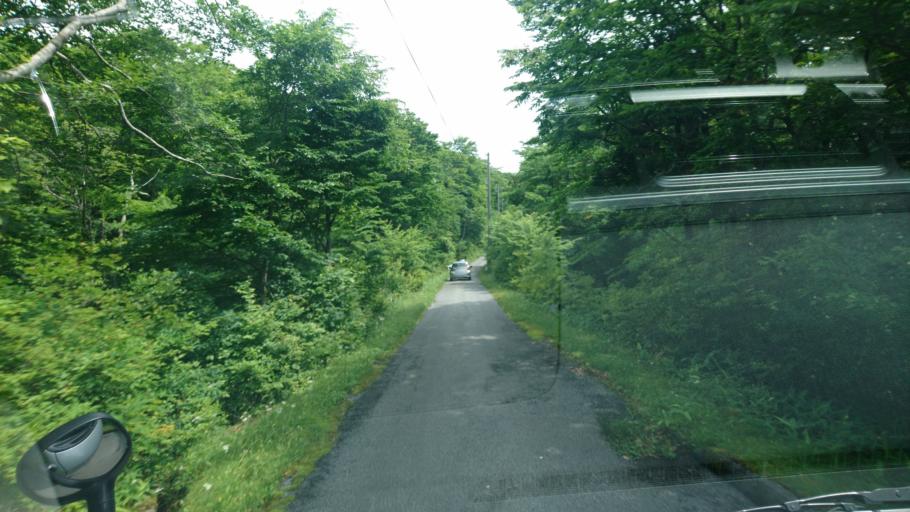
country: JP
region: Iwate
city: Ofunato
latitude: 39.1641
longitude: 141.7485
